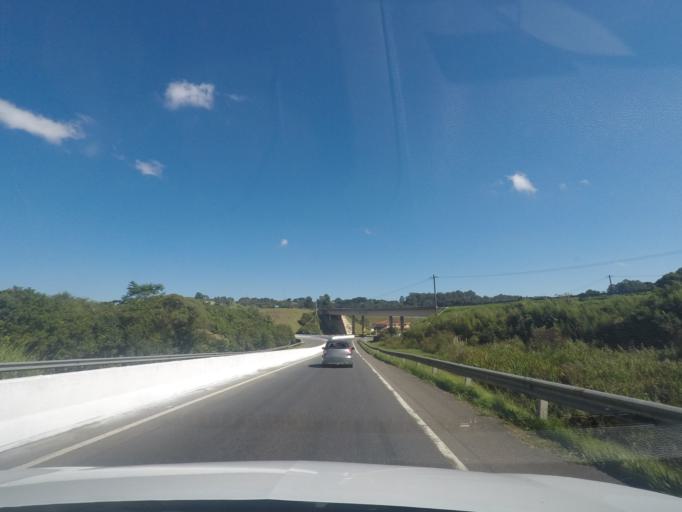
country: BR
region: Parana
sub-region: Almirante Tamandare
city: Almirante Tamandare
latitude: -25.3507
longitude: -49.2798
